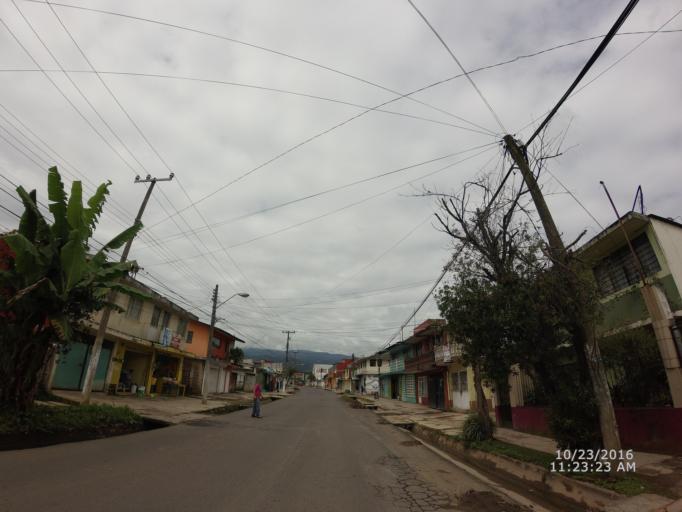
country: MX
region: Veracruz
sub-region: Tlalnelhuayocan
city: Guadalupe Victoria
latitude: 19.5508
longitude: -96.9493
